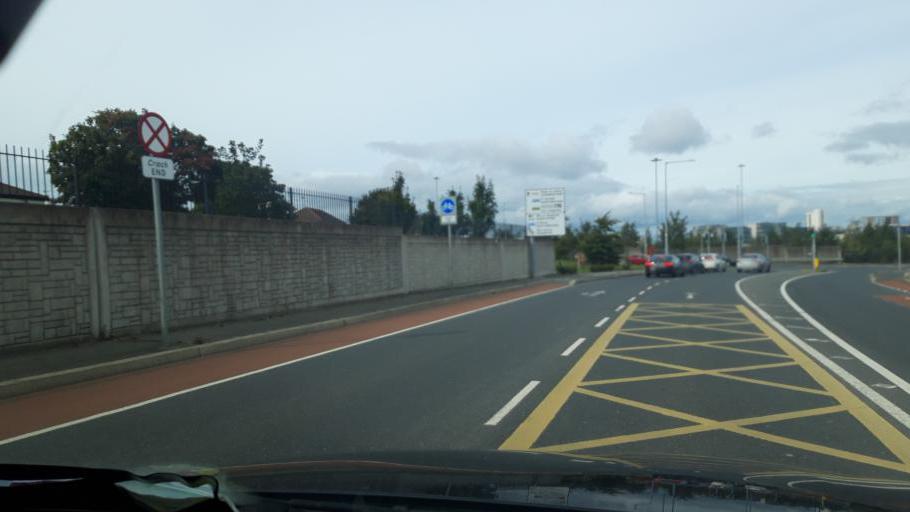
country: IE
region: Leinster
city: Sandyford
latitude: 53.2690
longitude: -6.2113
